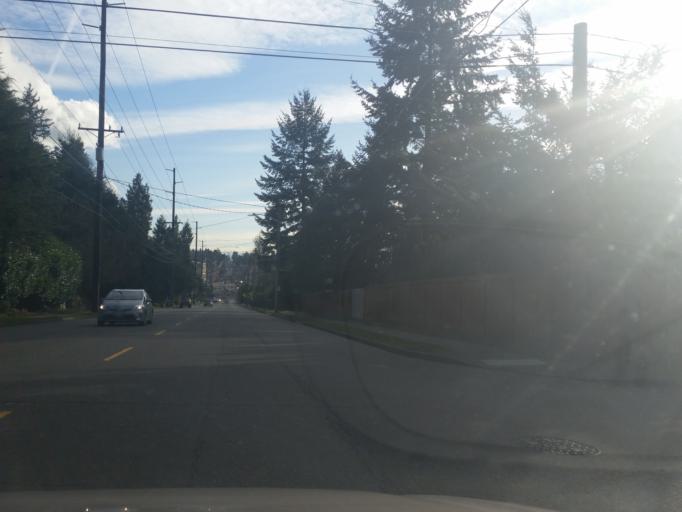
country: US
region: Washington
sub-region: King County
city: Shoreline
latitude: 47.7141
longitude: -122.3234
